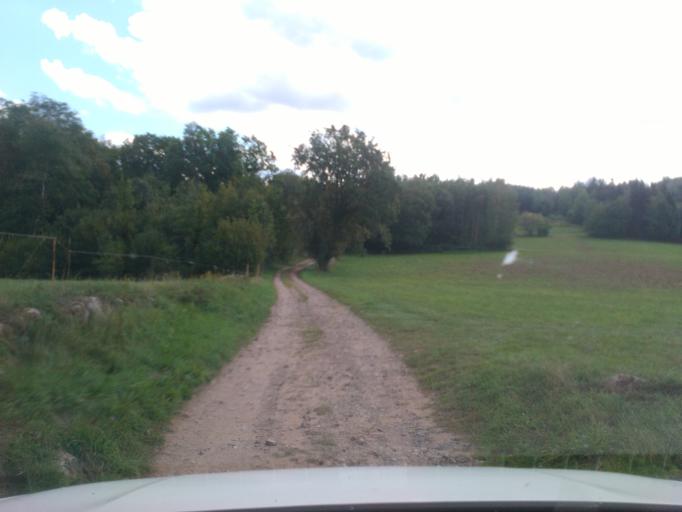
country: FR
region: Lorraine
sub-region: Departement des Vosges
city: Senones
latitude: 48.3887
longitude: 7.0135
